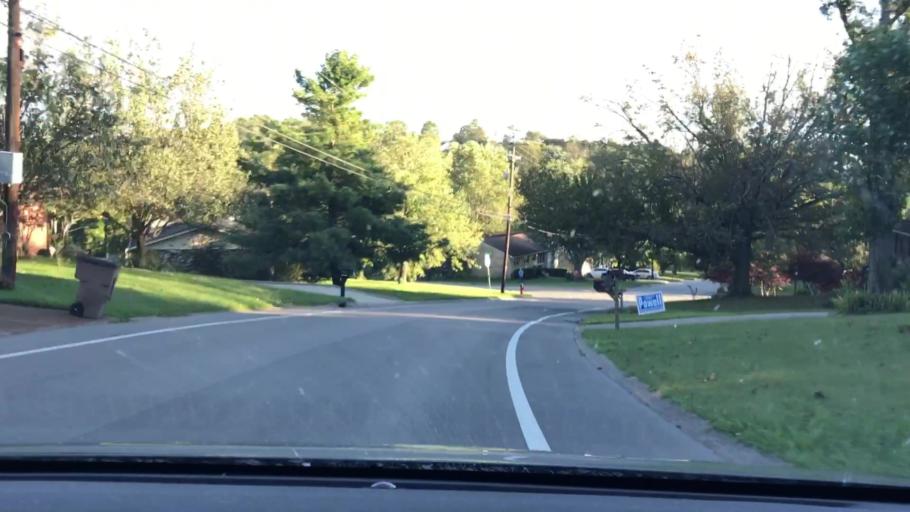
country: US
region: Tennessee
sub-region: Williamson County
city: Brentwood Estates
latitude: 36.0531
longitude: -86.7028
